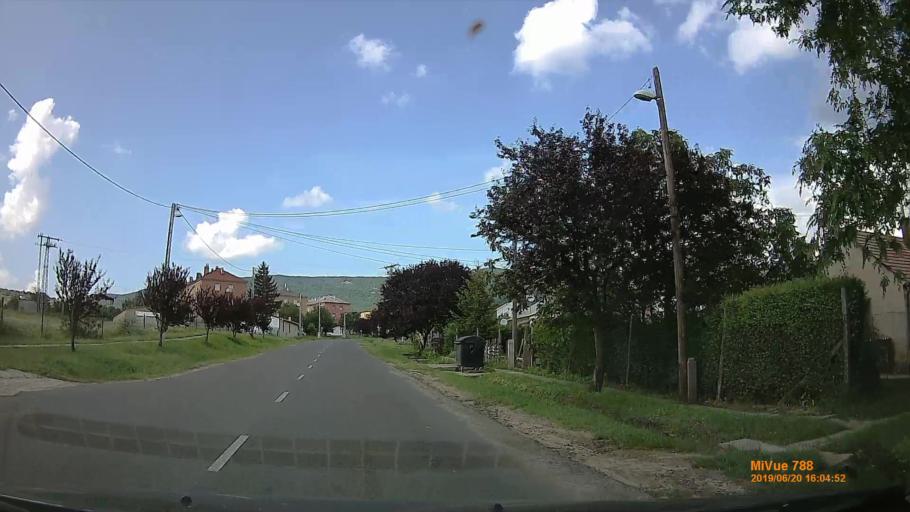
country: HU
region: Baranya
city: Pellerd
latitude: 46.0756
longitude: 18.1162
